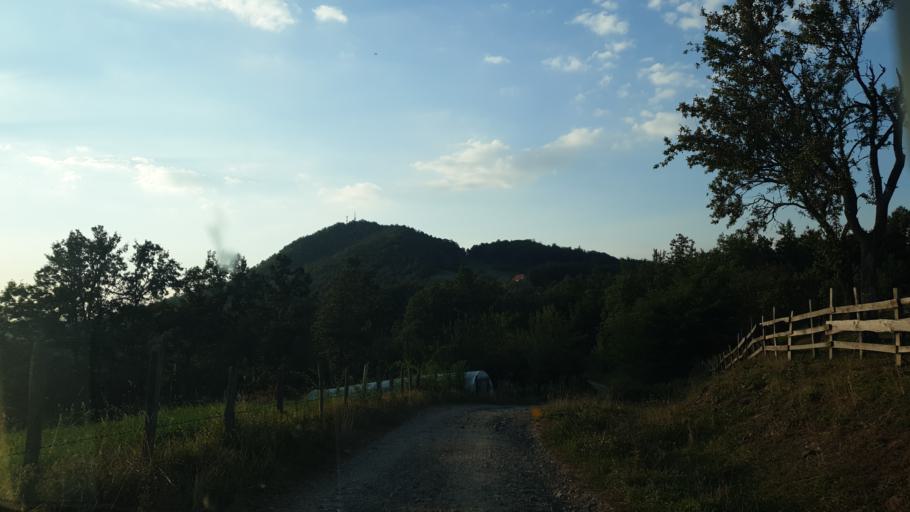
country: RS
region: Central Serbia
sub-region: Zlatiborski Okrug
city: Kosjeric
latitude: 44.0067
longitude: 19.9936
